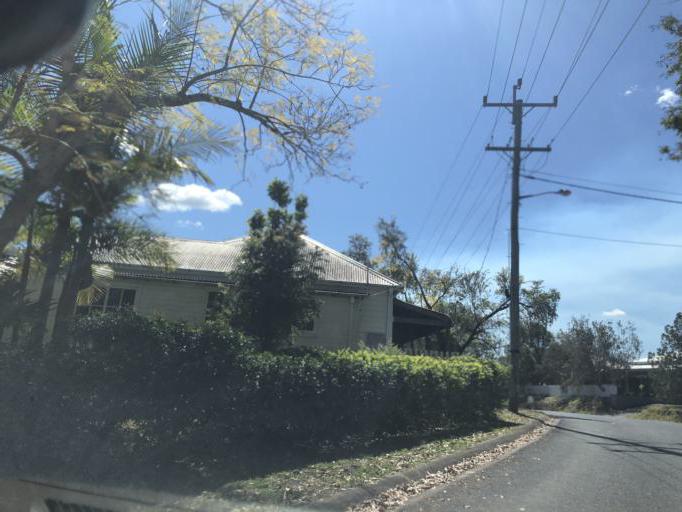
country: AU
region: New South Wales
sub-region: Bellingen
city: Bellingen
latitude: -30.4585
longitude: 152.8979
